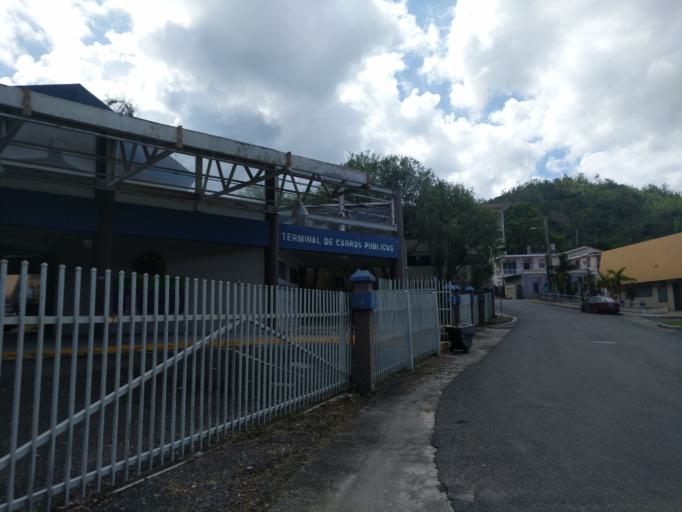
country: PR
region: Utuado
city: Utuado
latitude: 18.2663
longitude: -66.6976
